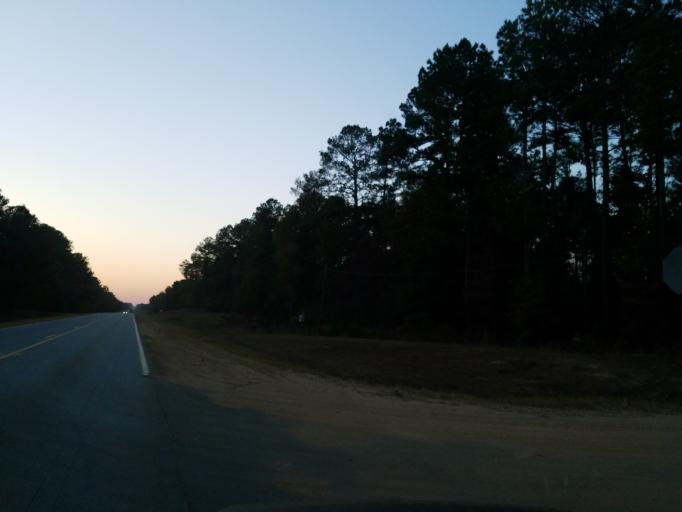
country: US
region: Georgia
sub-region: Turner County
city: Ashburn
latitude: 31.7213
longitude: -83.4808
